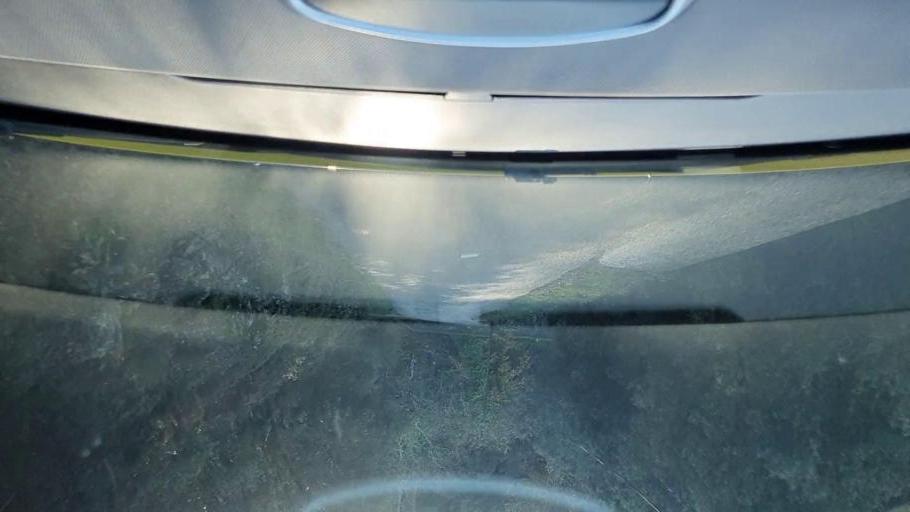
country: FR
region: Languedoc-Roussillon
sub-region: Departement du Gard
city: Lasalle
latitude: 44.0954
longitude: 3.8016
